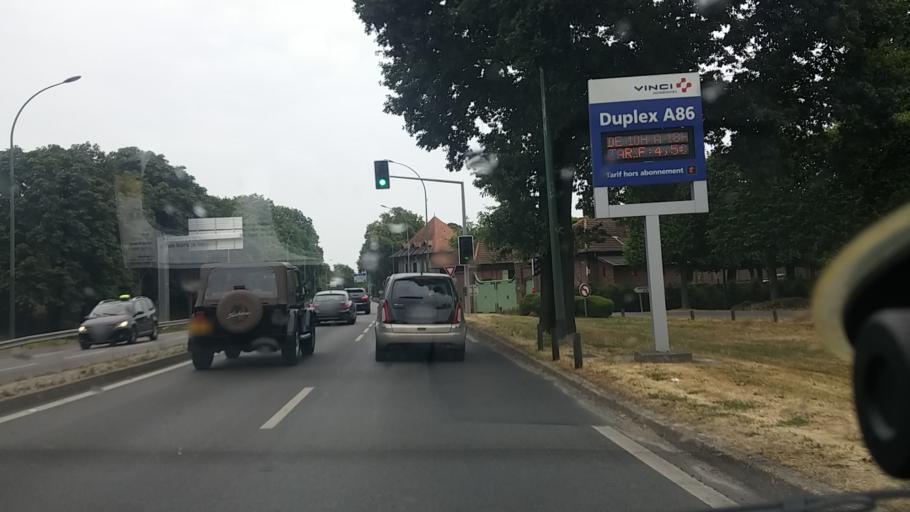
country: FR
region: Ile-de-France
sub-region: Departement des Hauts-de-Seine
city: Vaucresson
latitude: 48.8256
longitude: 2.1515
